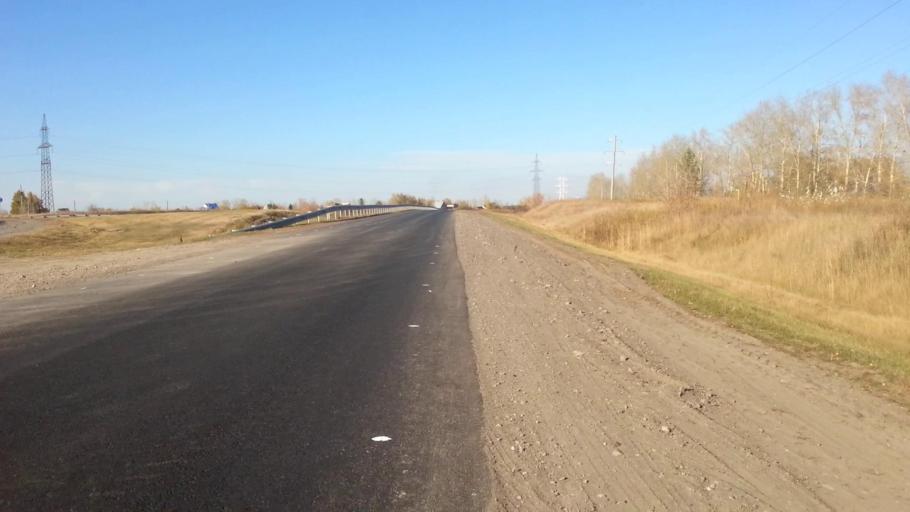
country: RU
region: Altai Krai
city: Sannikovo
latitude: 53.3391
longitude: 83.9387
